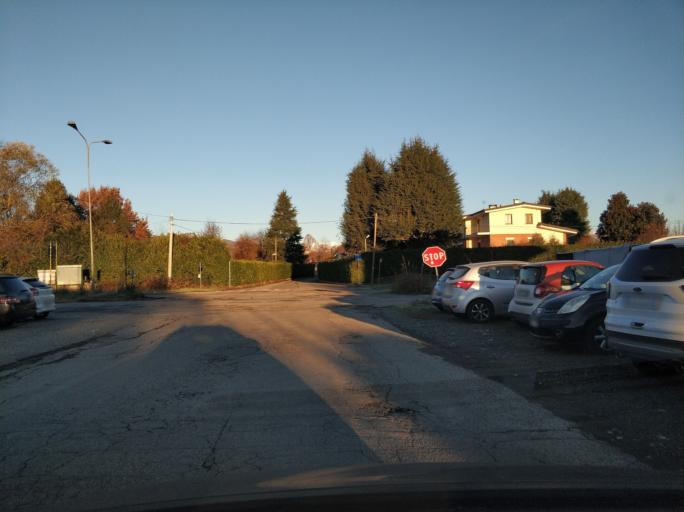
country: IT
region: Piedmont
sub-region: Provincia di Torino
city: Robassomero
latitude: 45.1791
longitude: 7.5901
